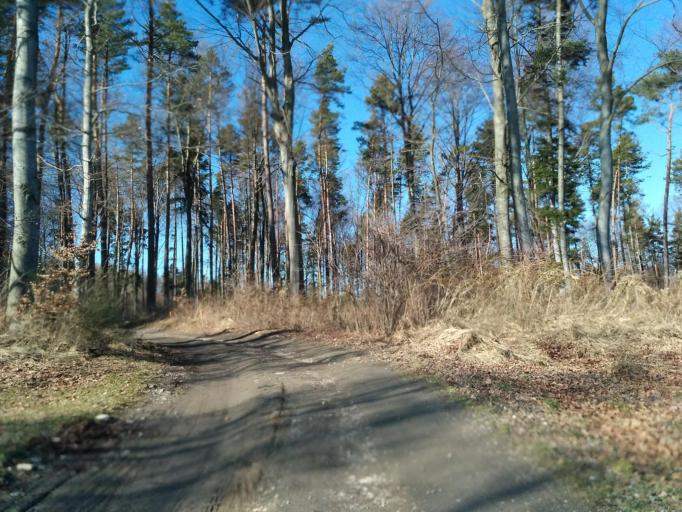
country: PL
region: Subcarpathian Voivodeship
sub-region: Powiat strzyzowski
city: Babica
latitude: 49.9519
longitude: 21.8836
